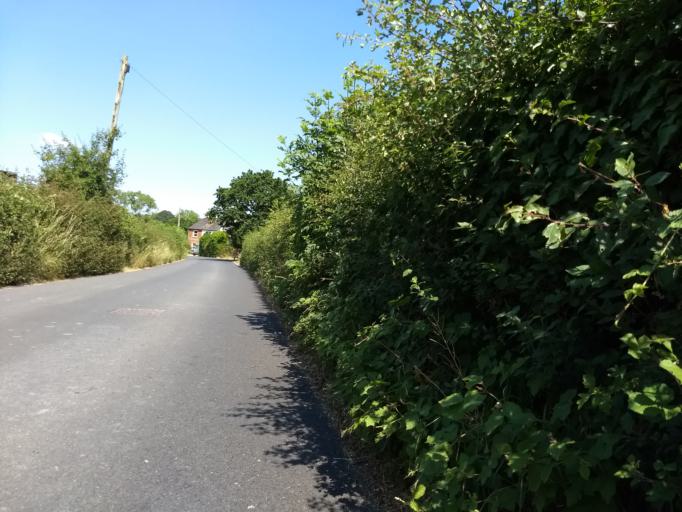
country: GB
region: England
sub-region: Isle of Wight
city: Shalfleet
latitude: 50.7197
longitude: -1.3667
